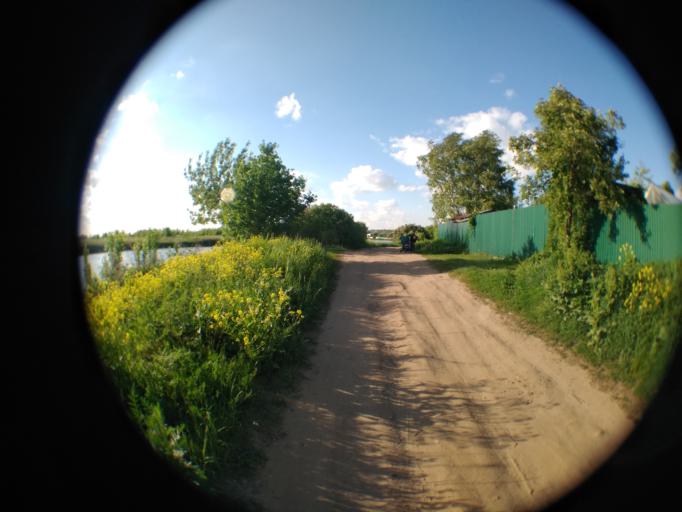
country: RU
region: Moskovskaya
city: Zhukovskiy
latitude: 55.5788
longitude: 38.1025
